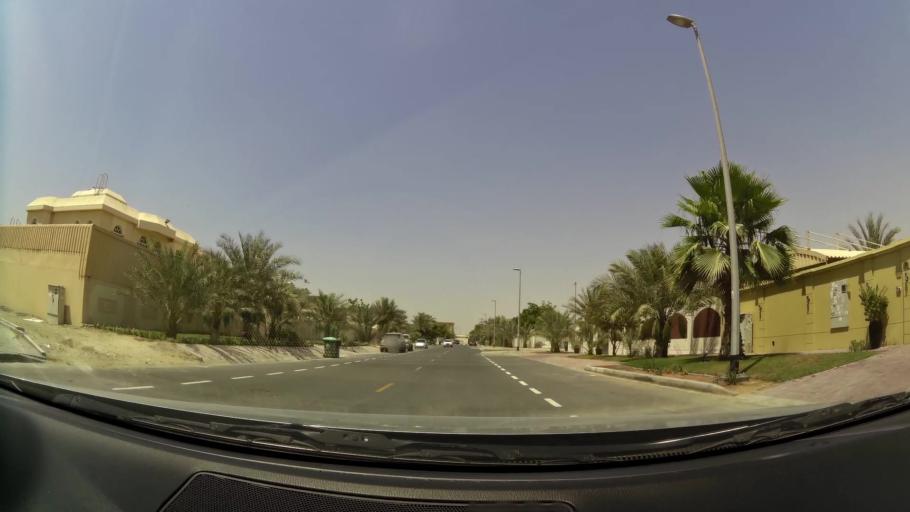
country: AE
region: Dubai
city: Dubai
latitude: 25.1029
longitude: 55.2153
